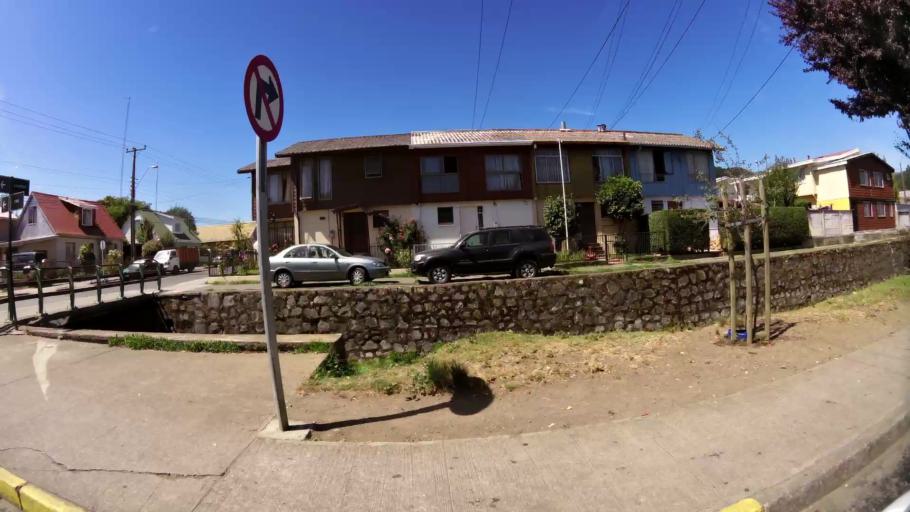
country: CL
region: Biobio
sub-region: Provincia de Concepcion
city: Penco
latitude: -36.7407
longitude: -72.9936
